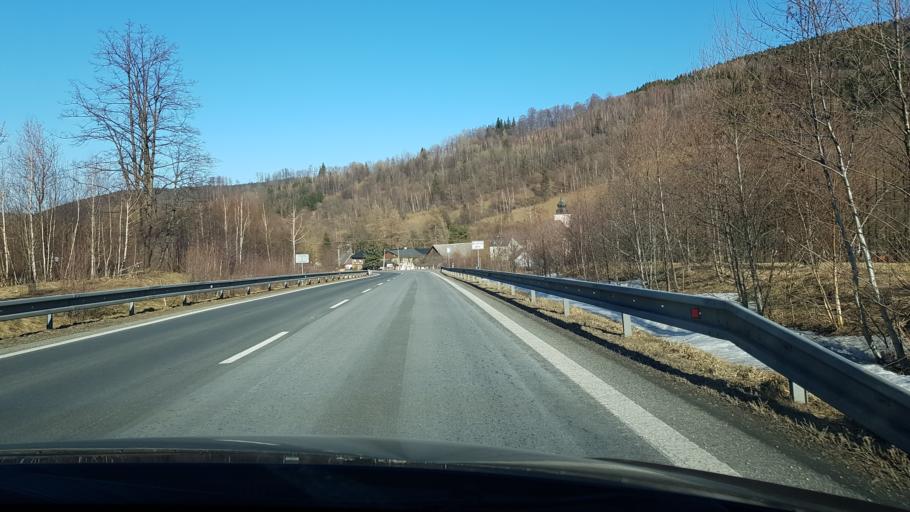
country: CZ
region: Olomoucky
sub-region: Okres Jesenik
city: Jesenik
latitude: 50.1594
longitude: 17.1916
